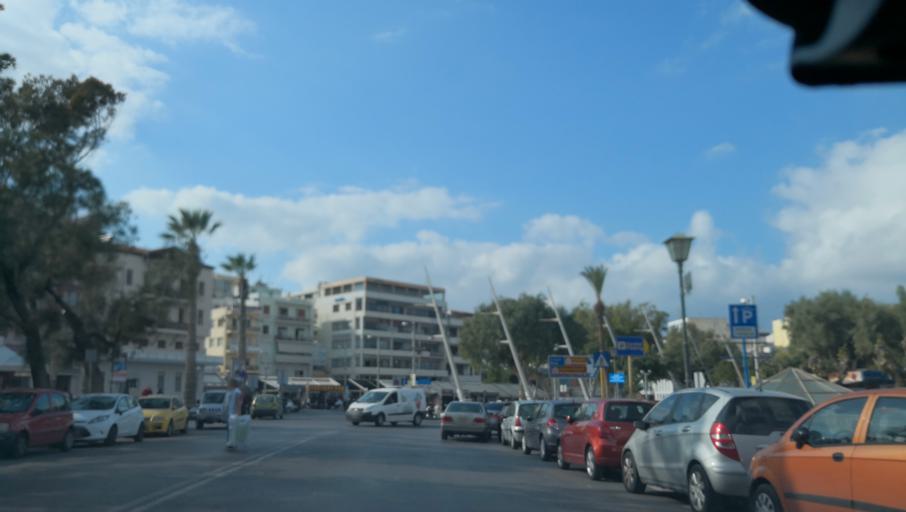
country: GR
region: Crete
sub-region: Nomos Irakleiou
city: Irakleion
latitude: 35.3371
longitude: 25.1372
